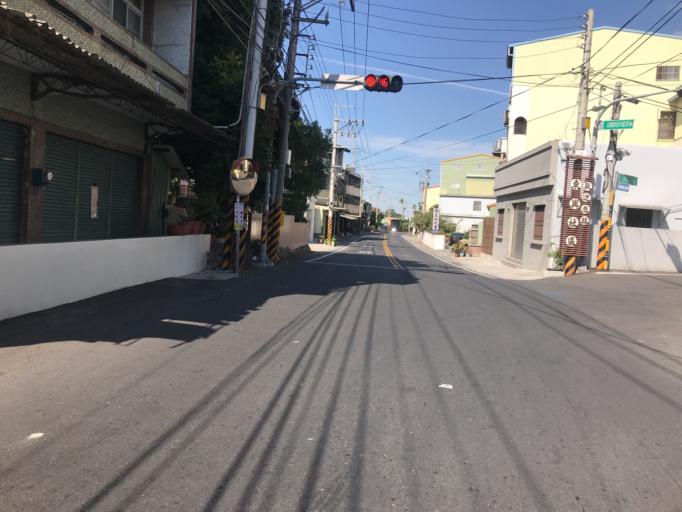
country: TW
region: Taiwan
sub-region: Nantou
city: Nantou
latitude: 23.8637
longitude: 120.6030
